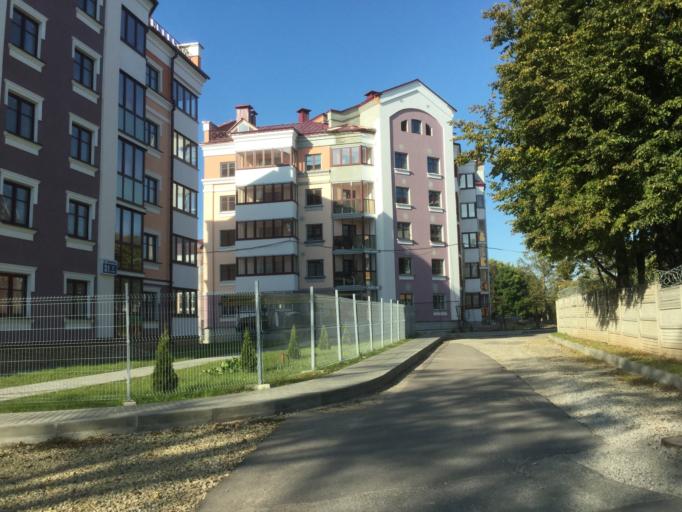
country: BY
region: Vitebsk
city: Vitebsk
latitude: 55.1723
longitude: 30.1948
